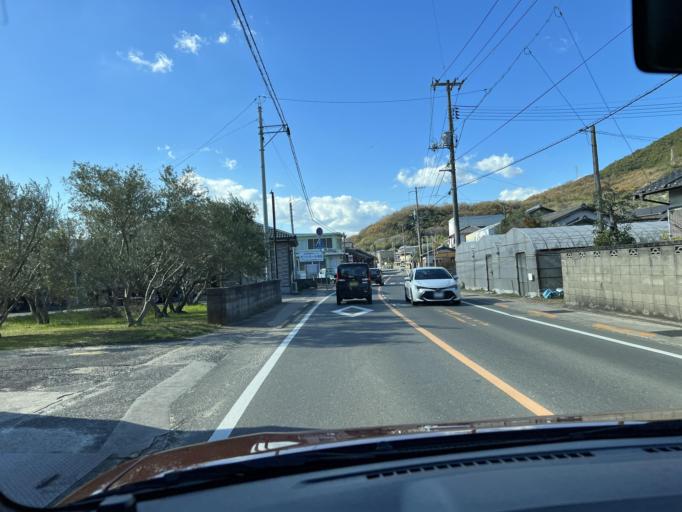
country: JP
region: Kagawa
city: Tonosho
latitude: 34.4824
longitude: 134.2316
